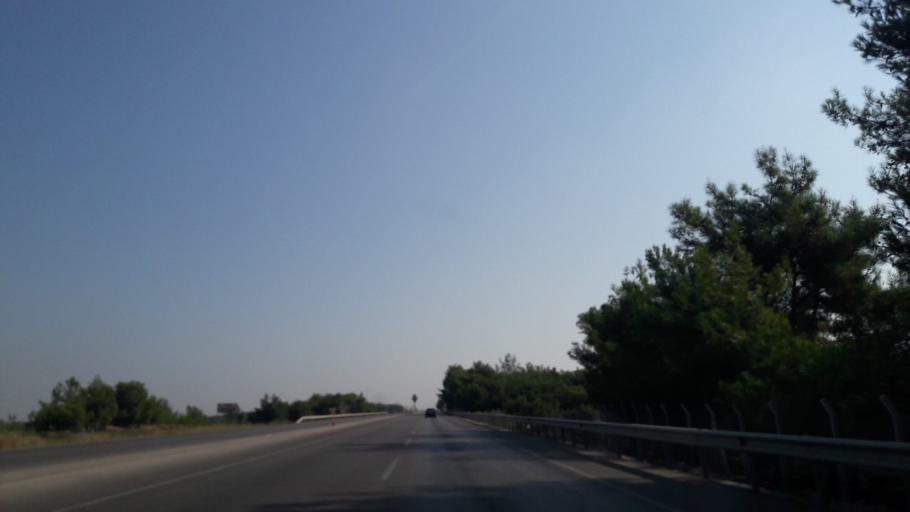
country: TR
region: Adana
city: Yuregir
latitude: 37.0881
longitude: 35.4883
